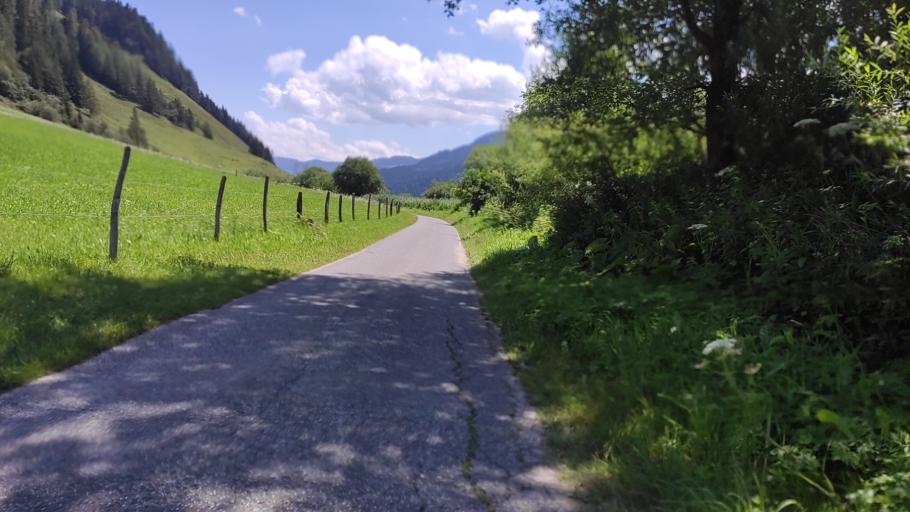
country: AT
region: Tyrol
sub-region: Politischer Bezirk Kitzbuhel
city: Hochfilzen
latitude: 47.4647
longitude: 12.6380
